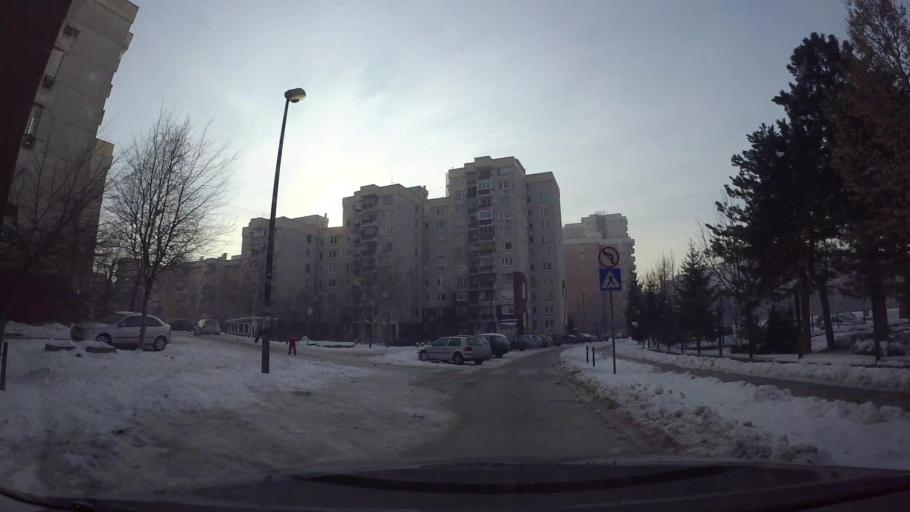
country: BA
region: Federation of Bosnia and Herzegovina
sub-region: Kanton Sarajevo
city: Sarajevo
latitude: 43.8433
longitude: 18.3452
